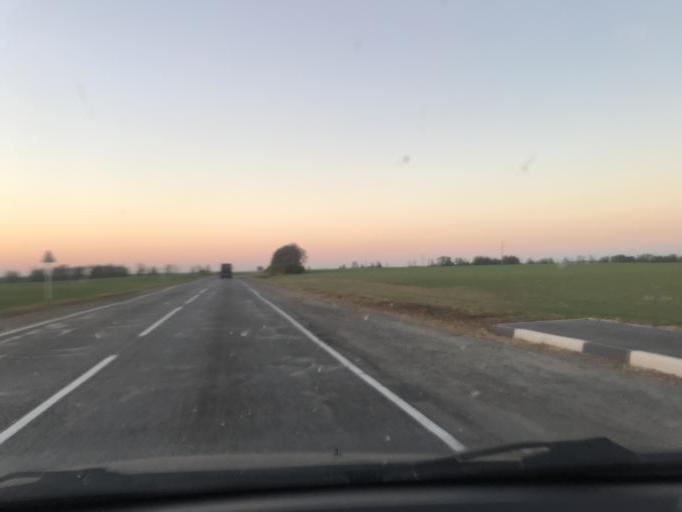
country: BY
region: Gomel
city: Horad Rechytsa
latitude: 52.2123
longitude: 30.5287
